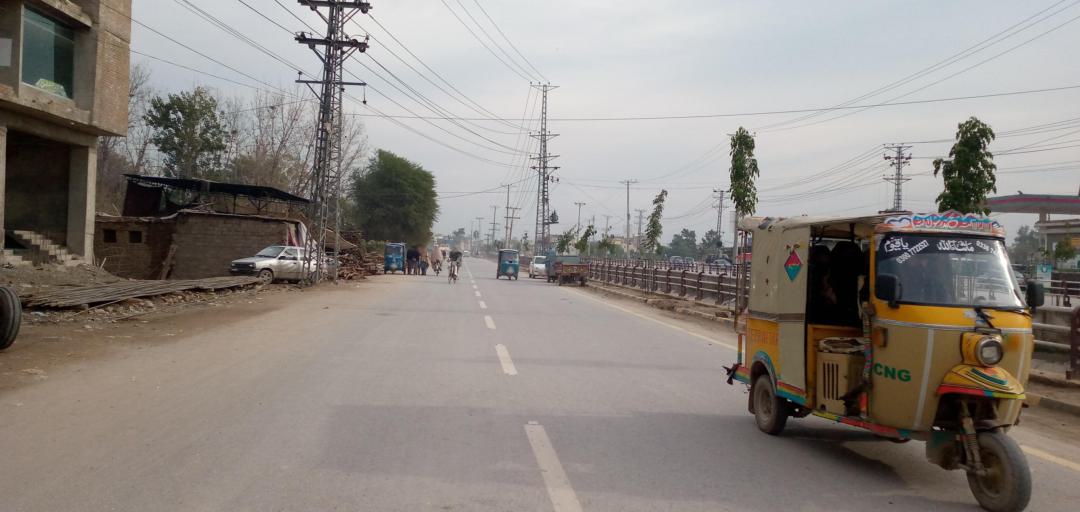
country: PK
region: Khyber Pakhtunkhwa
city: Peshawar
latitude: 34.0056
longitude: 71.4636
